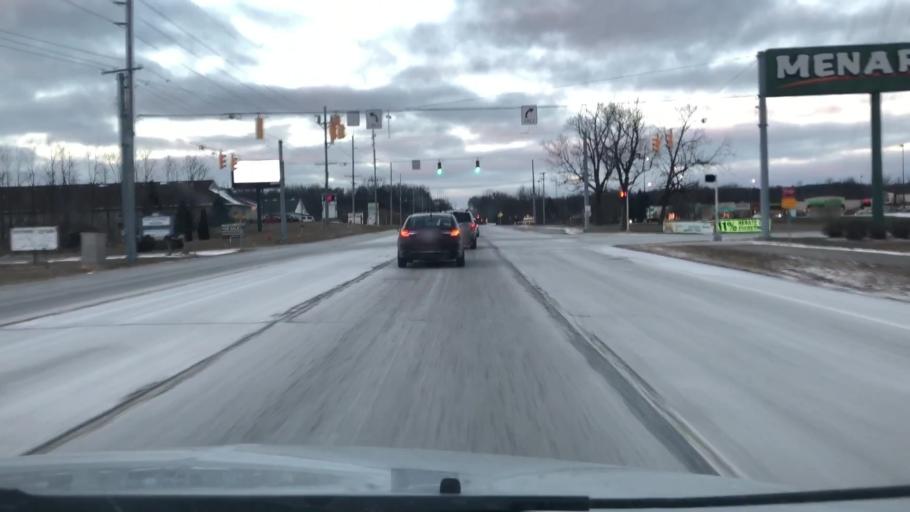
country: US
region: Indiana
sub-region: Steuben County
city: Angola
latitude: 41.6741
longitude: -84.9996
